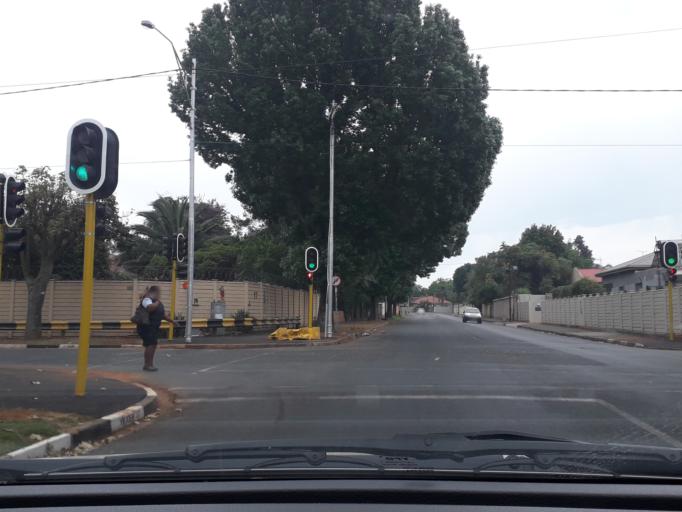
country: ZA
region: Gauteng
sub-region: City of Johannesburg Metropolitan Municipality
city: Johannesburg
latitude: -26.1489
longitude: 28.0903
